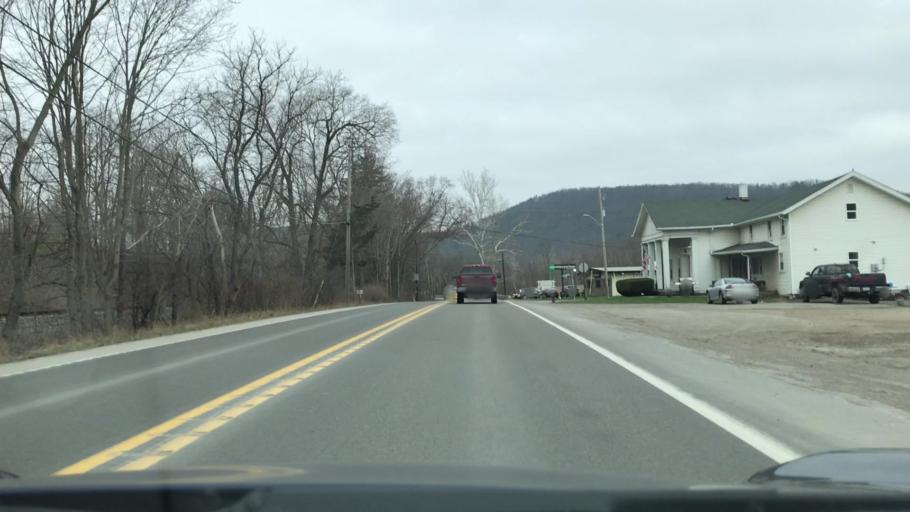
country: US
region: Pennsylvania
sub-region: Bradford County
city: Towanda
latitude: 41.7770
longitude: -76.3798
